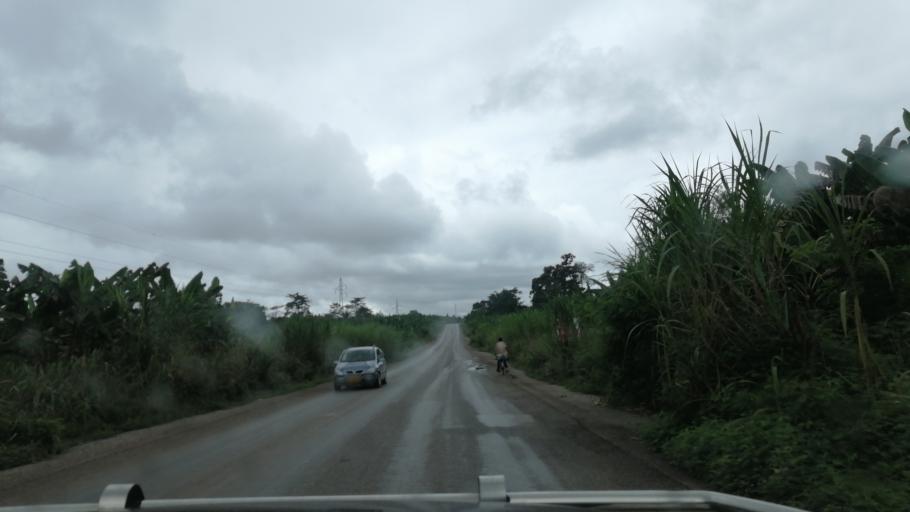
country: GH
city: Duayaw Nkwanta
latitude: 6.9078
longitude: -2.3954
